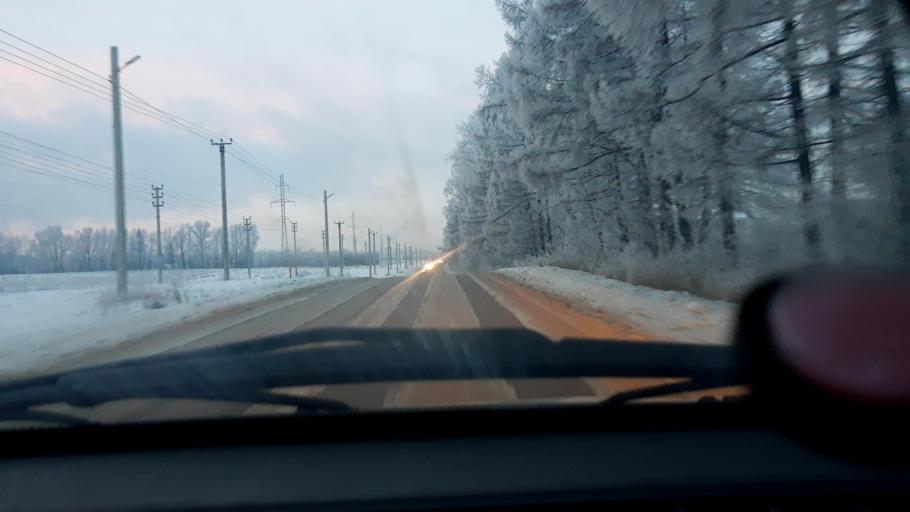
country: RU
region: Bashkortostan
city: Mikhaylovka
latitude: 54.8287
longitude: 55.8780
